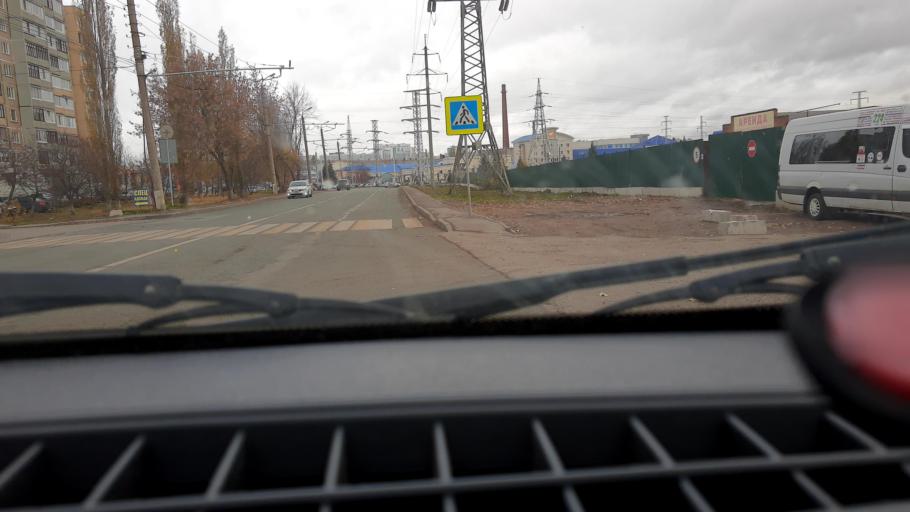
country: RU
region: Bashkortostan
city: Ufa
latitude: 54.7951
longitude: 56.0563
